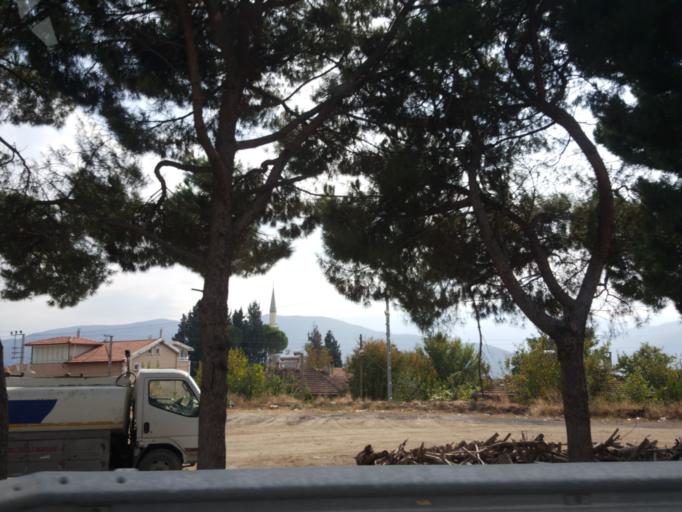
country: TR
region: Corum
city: Hacihamza
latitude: 41.1227
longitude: 34.4156
